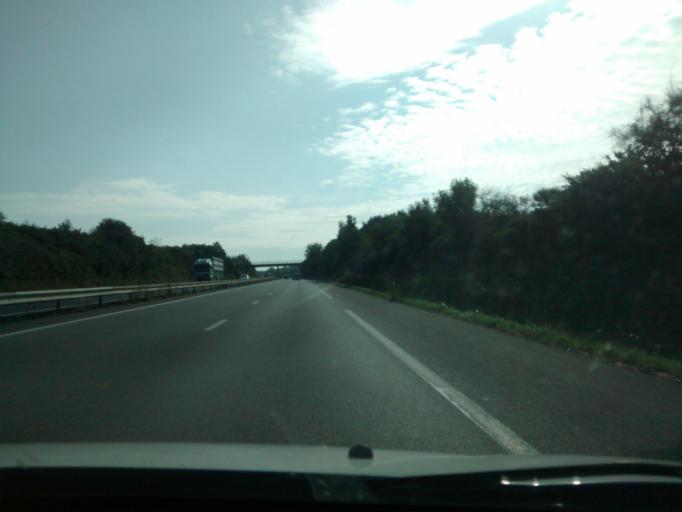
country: FR
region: Brittany
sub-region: Departement d'Ille-et-Vilaine
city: Argentre-du-Plessis
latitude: 48.0706
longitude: -1.1686
